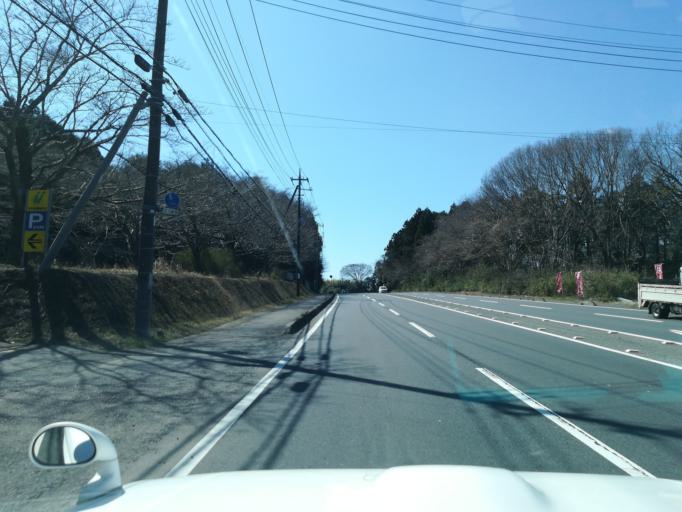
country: JP
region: Ibaraki
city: Ushiku
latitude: 35.9663
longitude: 140.1712
